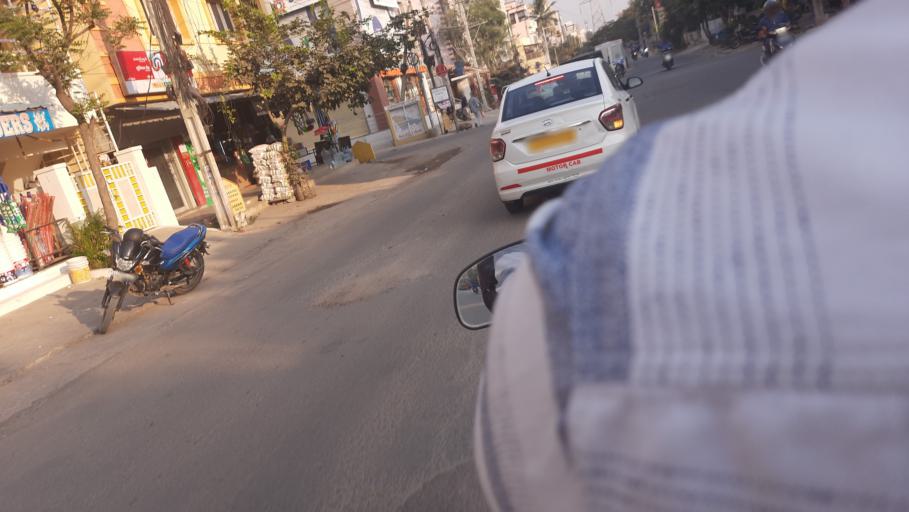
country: IN
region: Telangana
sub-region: Rangareddi
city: Secunderabad
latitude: 17.4901
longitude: 78.5498
